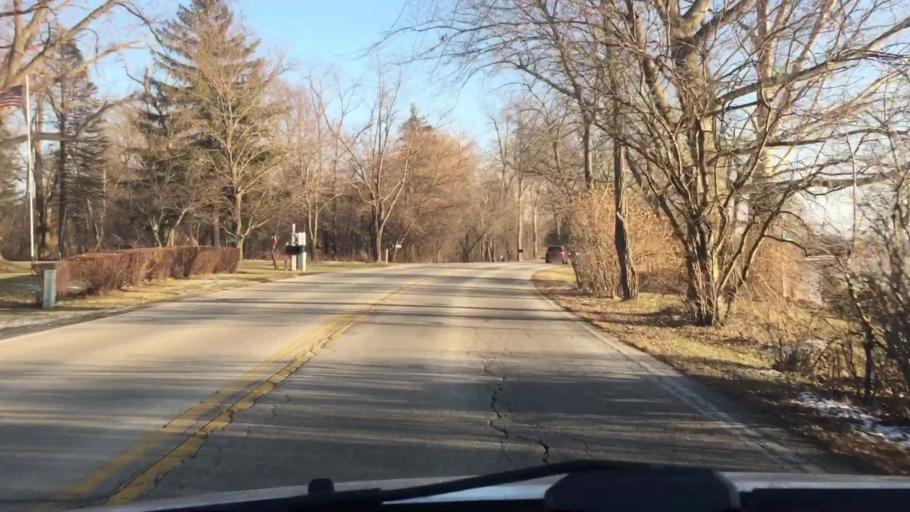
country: US
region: Wisconsin
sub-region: Waukesha County
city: Oconomowoc
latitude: 43.0811
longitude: -88.4928
